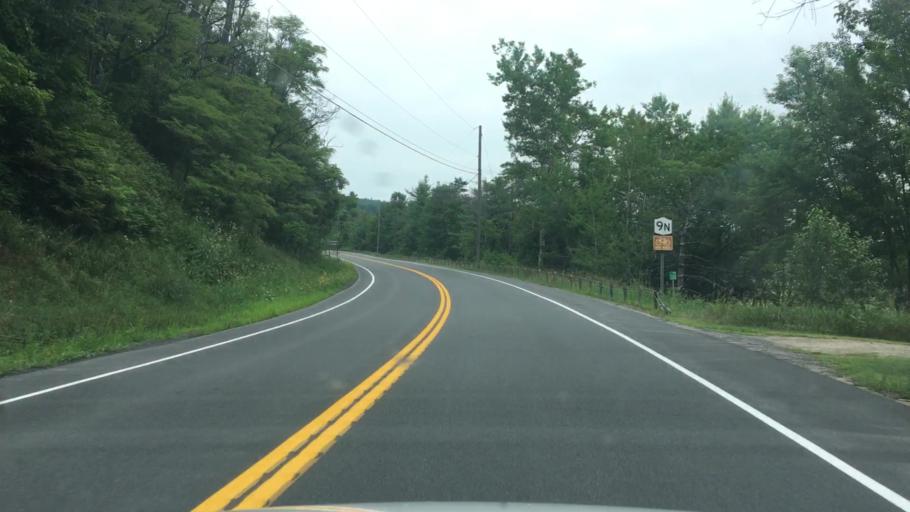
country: US
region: New York
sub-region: Essex County
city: Keeseville
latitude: 44.4681
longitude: -73.5723
